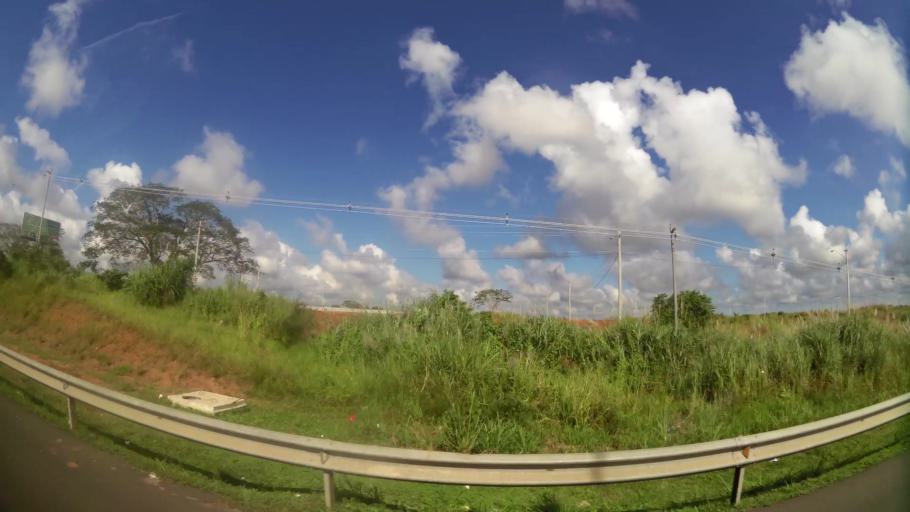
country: PA
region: Panama
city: Nuevo Arraijan
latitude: 8.8964
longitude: -79.7453
